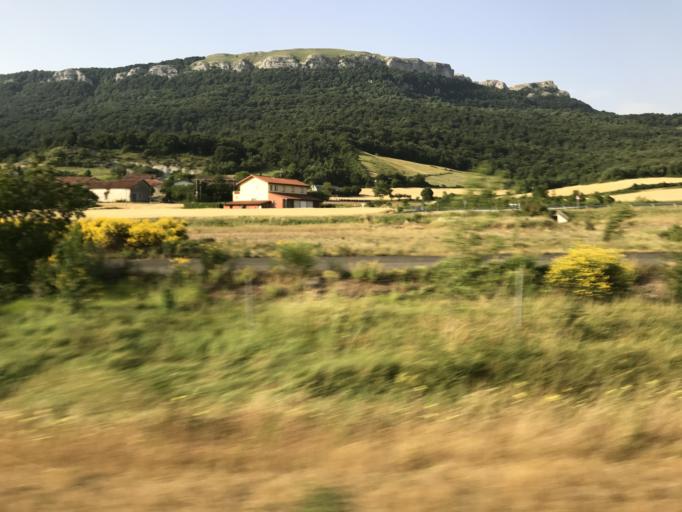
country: ES
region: Basque Country
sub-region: Provincia de Alava
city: Araya
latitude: 42.8661
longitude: -2.2953
